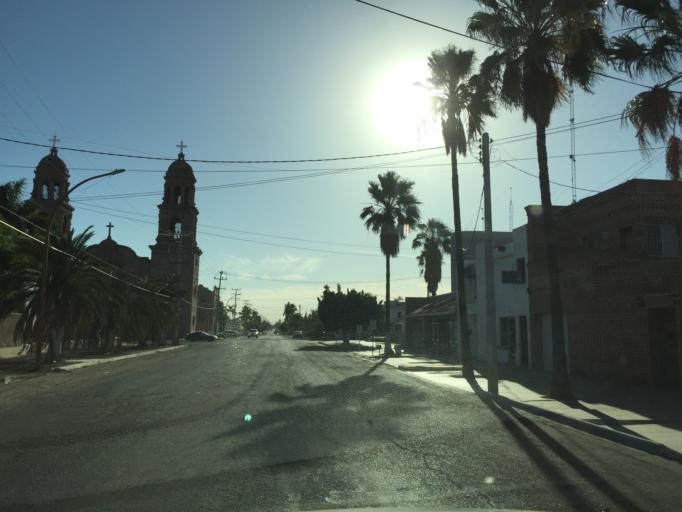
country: MX
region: Sonora
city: Navojoa
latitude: 27.0825
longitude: -109.4467
